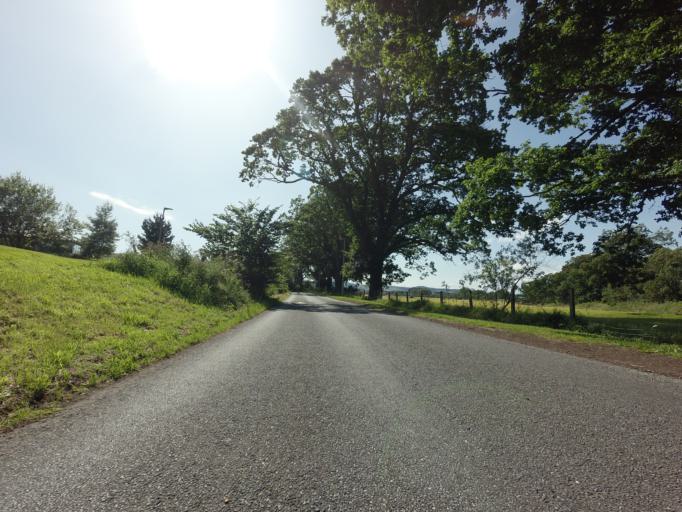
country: GB
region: Scotland
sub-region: Highland
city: Inverness
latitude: 57.4737
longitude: -4.1701
